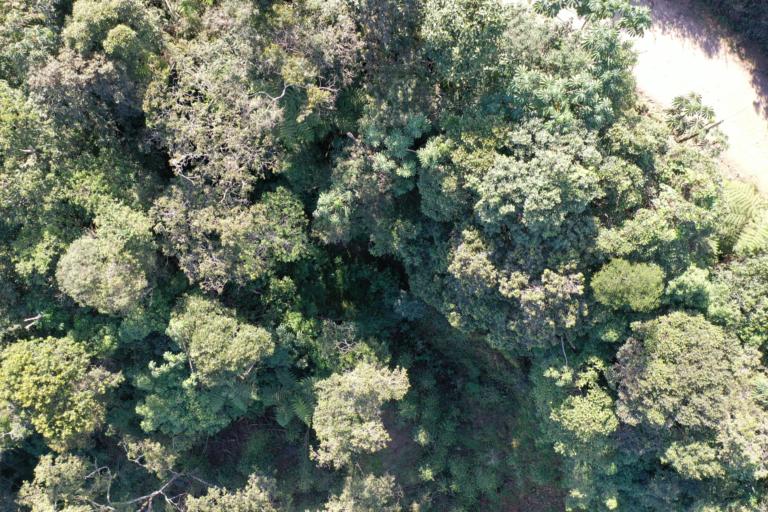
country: BO
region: La Paz
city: Coroico
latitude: -16.2557
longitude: -67.6976
